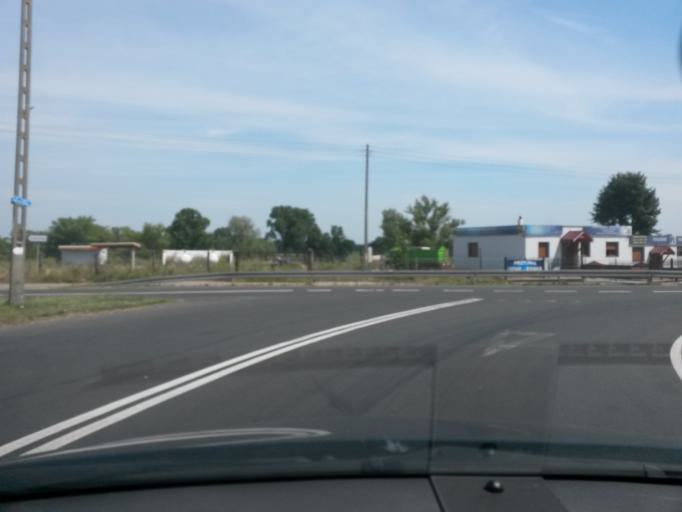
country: PL
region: Lower Silesian Voivodeship
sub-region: Powiat lubinski
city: Scinawa
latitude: 51.4099
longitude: 16.4383
